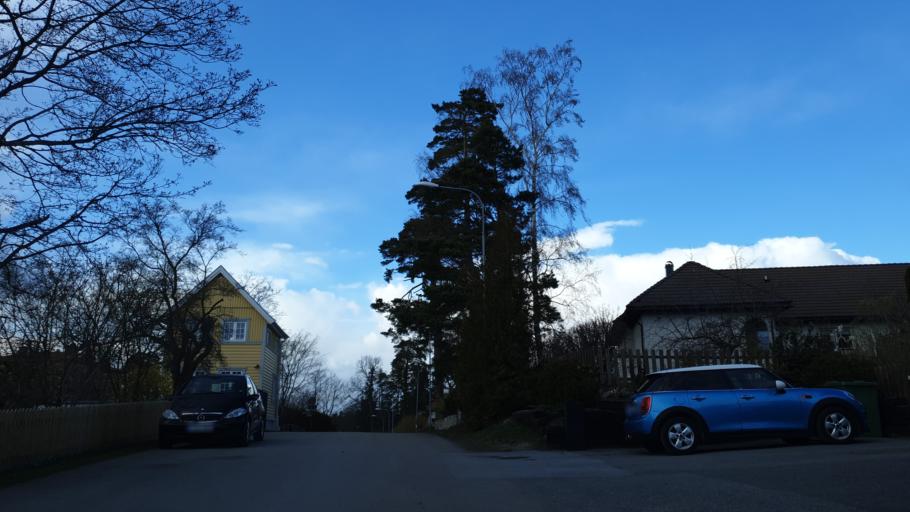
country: SE
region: Stockholm
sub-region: Lidingo
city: Lidingoe
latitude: 59.3683
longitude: 18.1412
